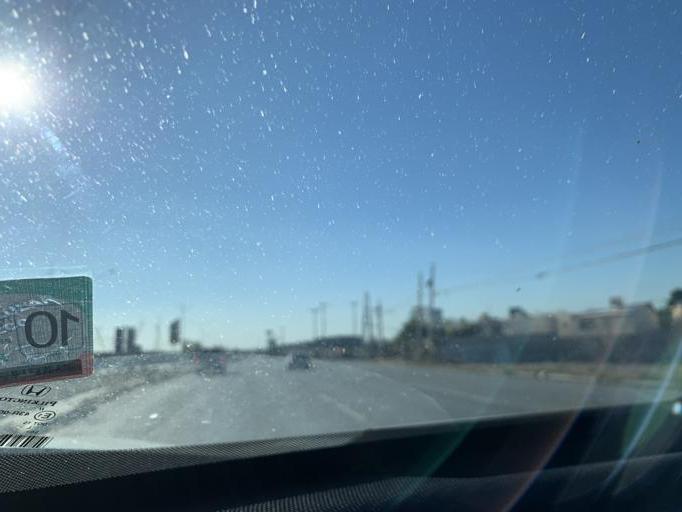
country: MX
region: Chihuahua
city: Ciudad Juarez
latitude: 31.6887
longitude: -106.3982
